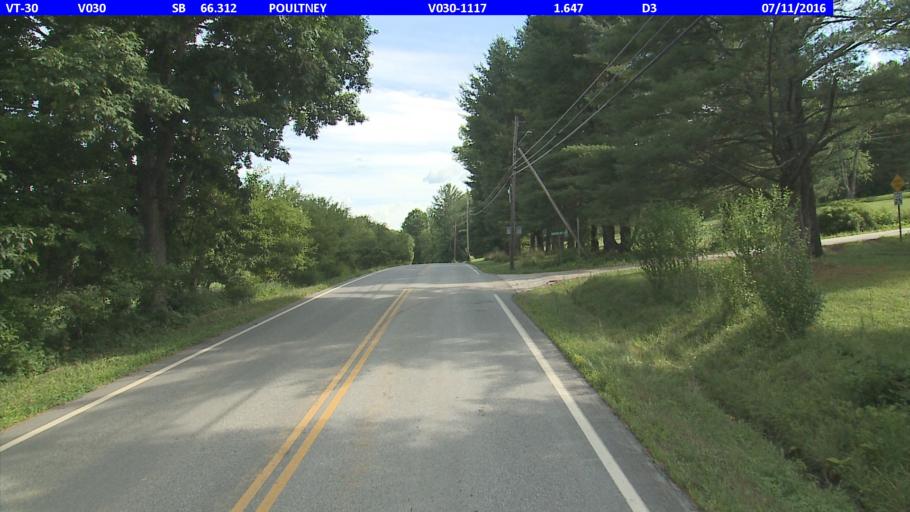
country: US
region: Vermont
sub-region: Rutland County
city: Poultney
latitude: 43.4871
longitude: -73.2028
